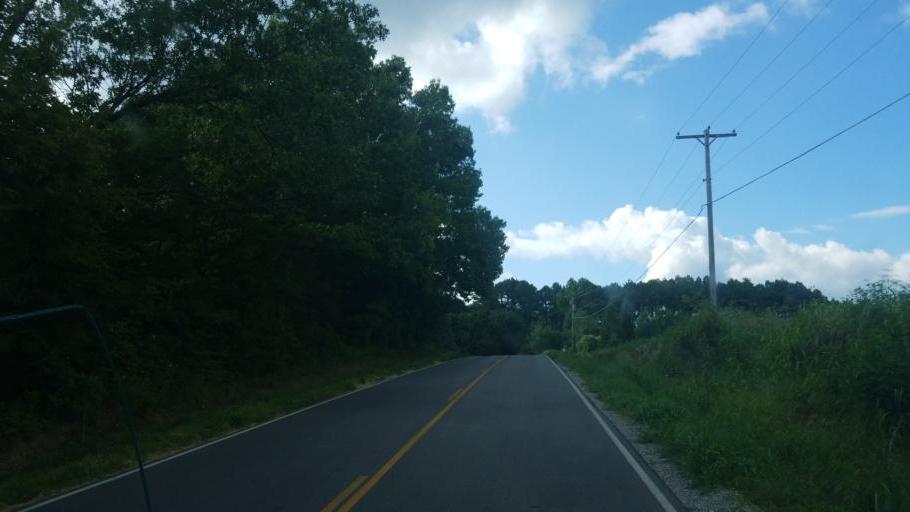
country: US
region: Illinois
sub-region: Union County
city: Cobden
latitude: 37.5670
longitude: -89.3116
